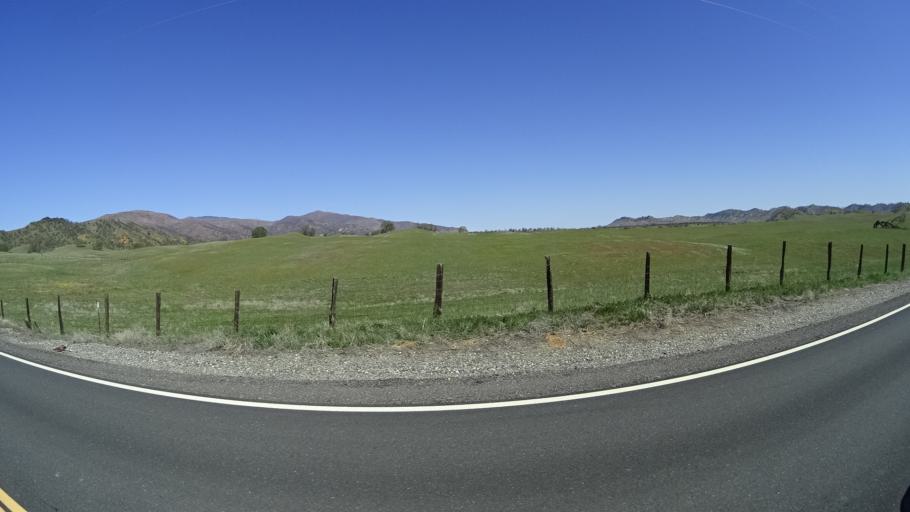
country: US
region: California
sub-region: Glenn County
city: Orland
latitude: 39.6572
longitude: -122.5582
